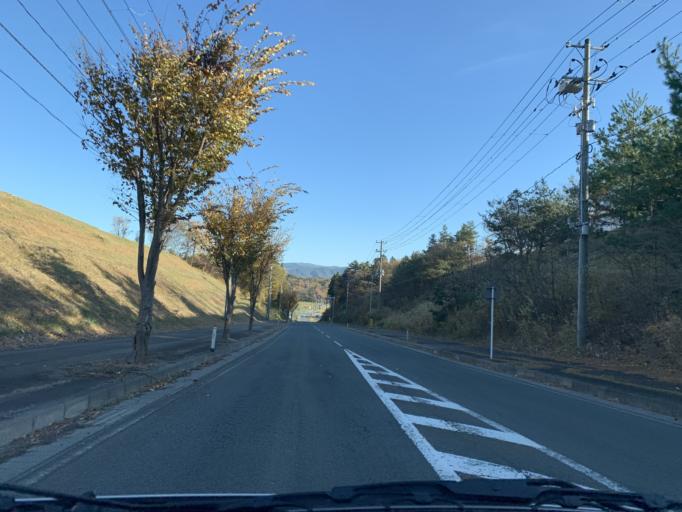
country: JP
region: Iwate
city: Mizusawa
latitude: 39.2062
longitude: 141.1833
